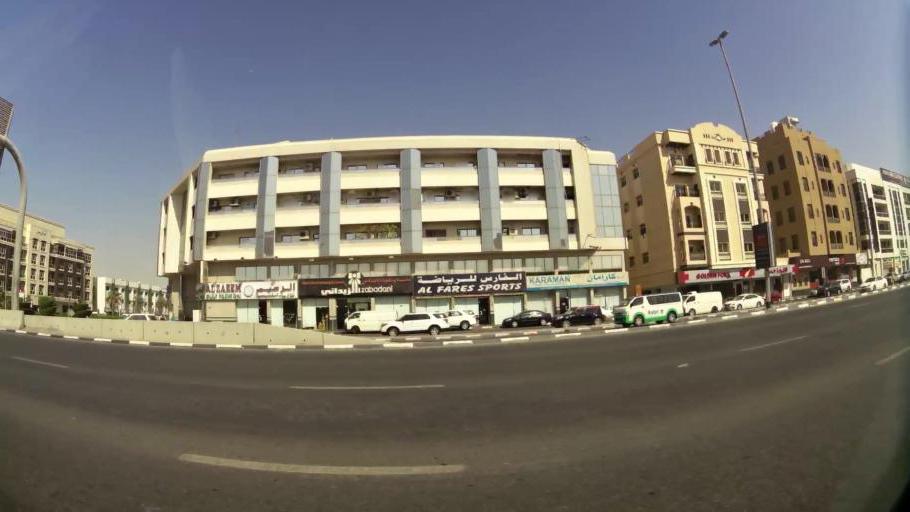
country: AE
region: Ash Shariqah
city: Sharjah
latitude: 25.2700
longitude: 55.3792
